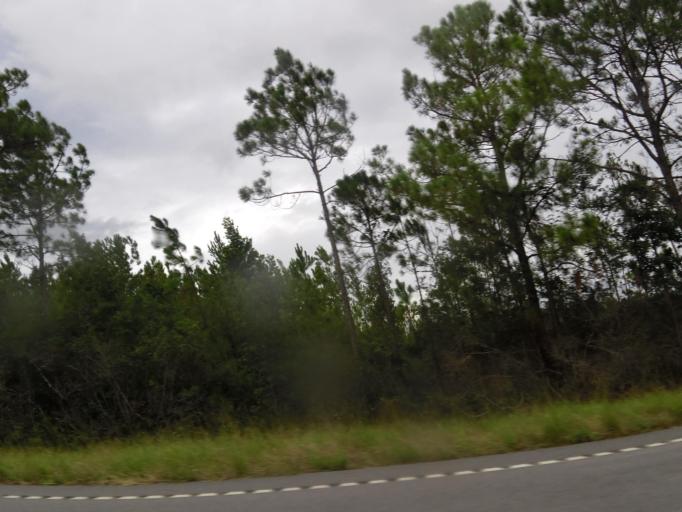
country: US
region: Florida
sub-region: Nassau County
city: Hilliard
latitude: 30.5217
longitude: -82.0641
